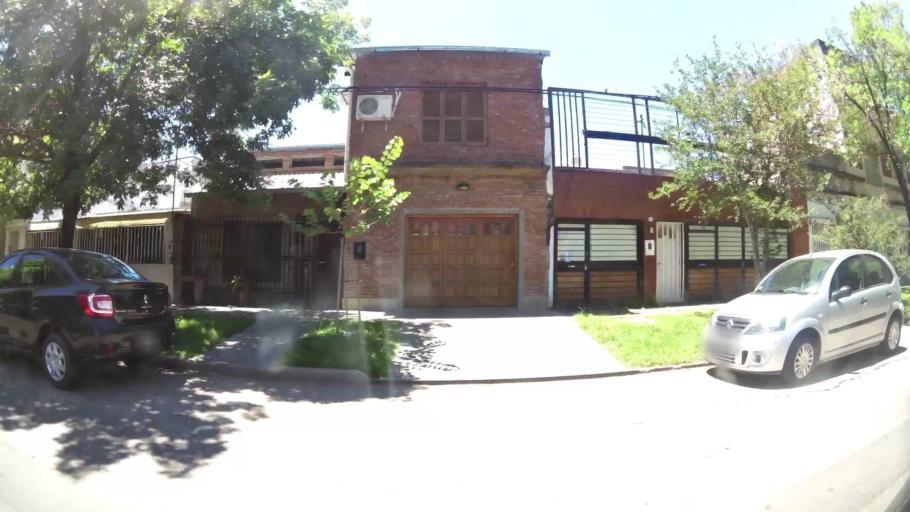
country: AR
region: Santa Fe
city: Santa Fe de la Vera Cruz
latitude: -31.6302
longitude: -60.7073
